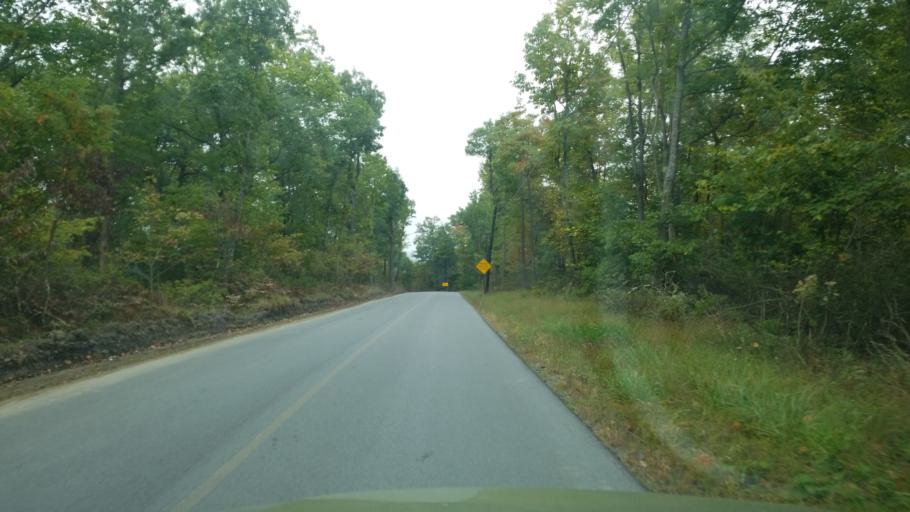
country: US
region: Pennsylvania
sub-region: Clearfield County
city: Curwensville
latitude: 41.0297
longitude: -78.5576
